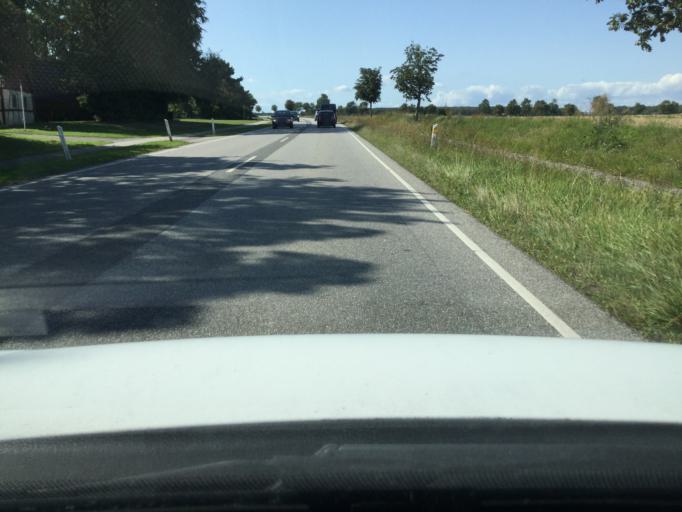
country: DK
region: Zealand
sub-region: Lolland Kommune
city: Nakskov
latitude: 54.8130
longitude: 11.1964
